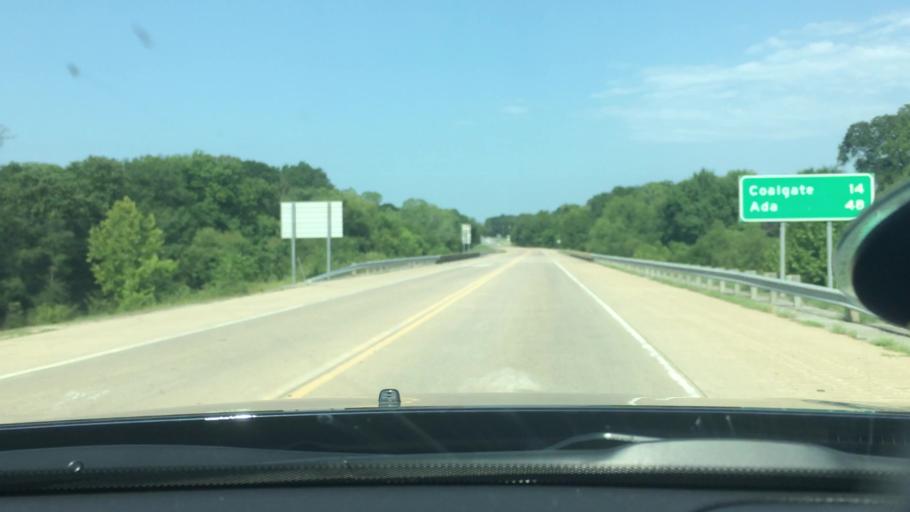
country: US
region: Oklahoma
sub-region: Atoka County
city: Atoka
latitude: 34.3932
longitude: -96.1267
